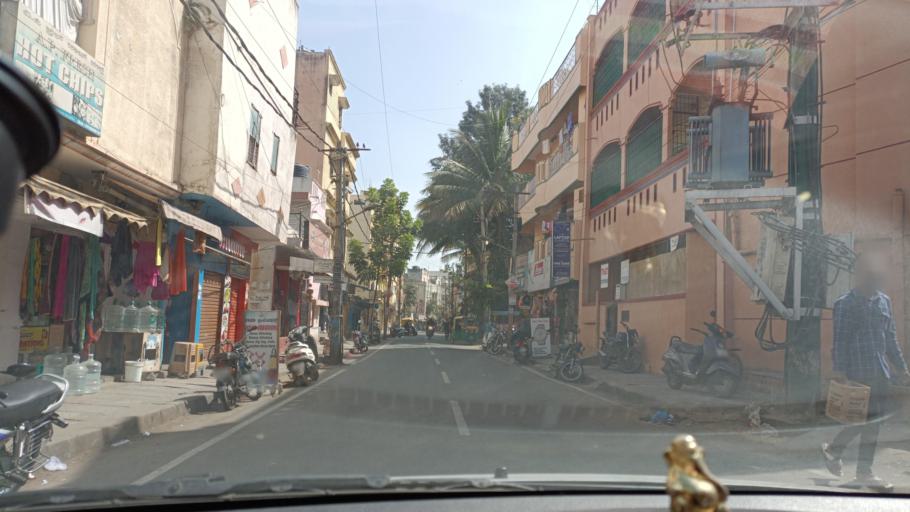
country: IN
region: Karnataka
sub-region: Bangalore Urban
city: Bangalore
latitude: 12.9204
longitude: 77.6163
